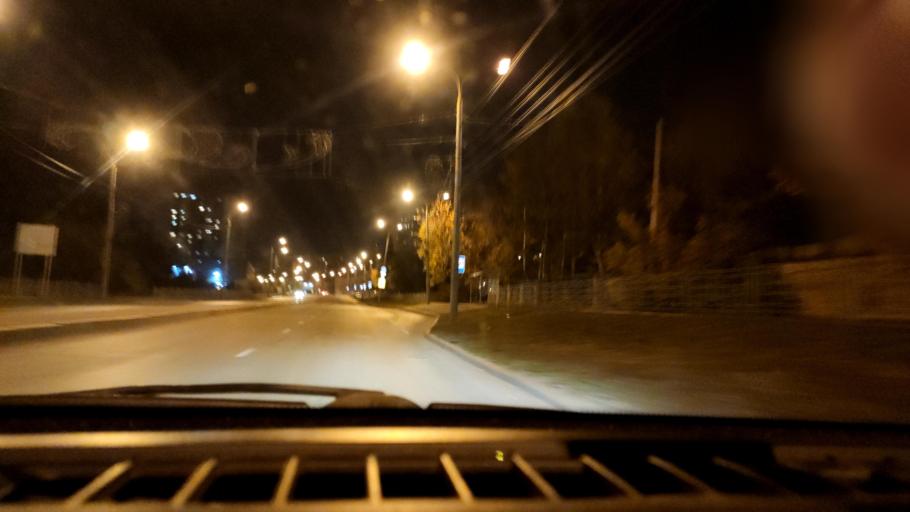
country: RU
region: Samara
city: Samara
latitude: 53.2467
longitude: 50.1958
